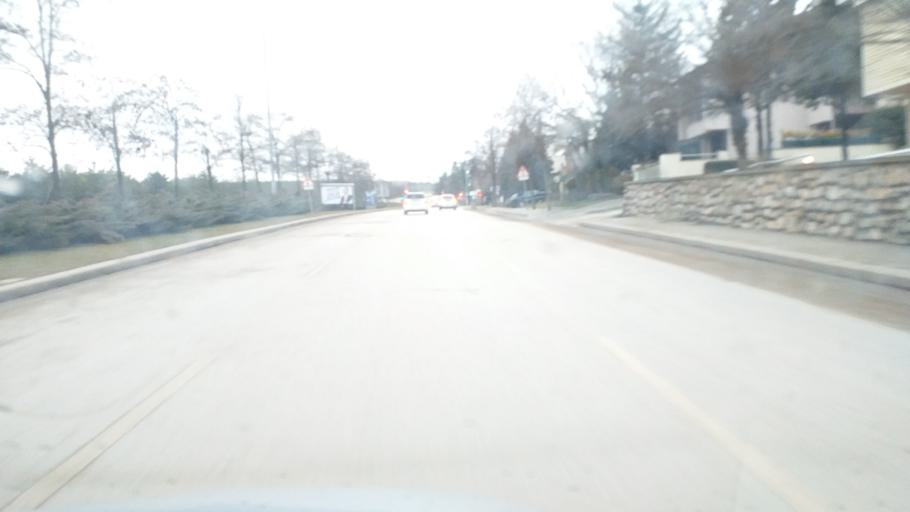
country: TR
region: Ankara
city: Batikent
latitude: 39.8950
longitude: 32.7302
